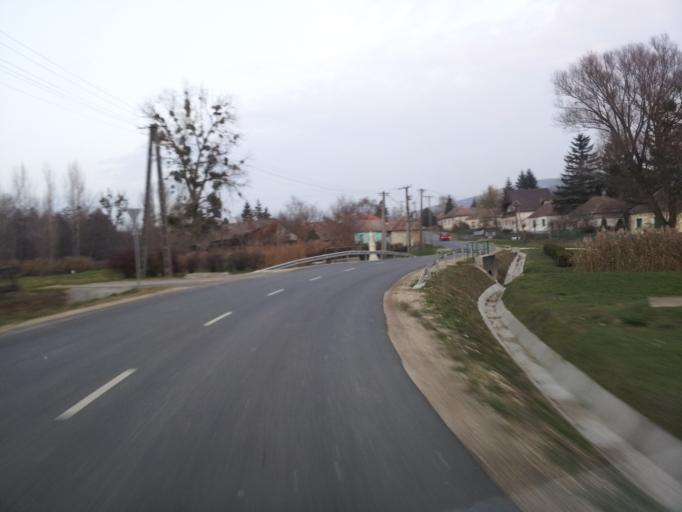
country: HU
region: Zala
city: Zalaszentgrot
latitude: 46.8954
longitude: 17.1522
